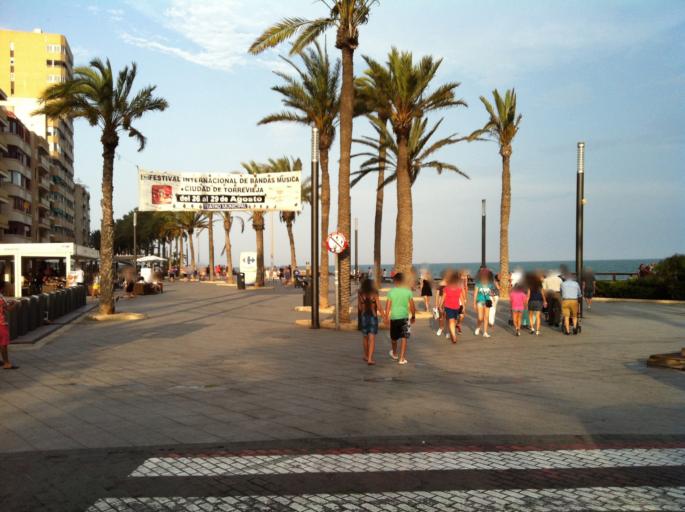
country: ES
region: Valencia
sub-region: Provincia de Alicante
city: Torrevieja
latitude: 37.9741
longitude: -0.6783
